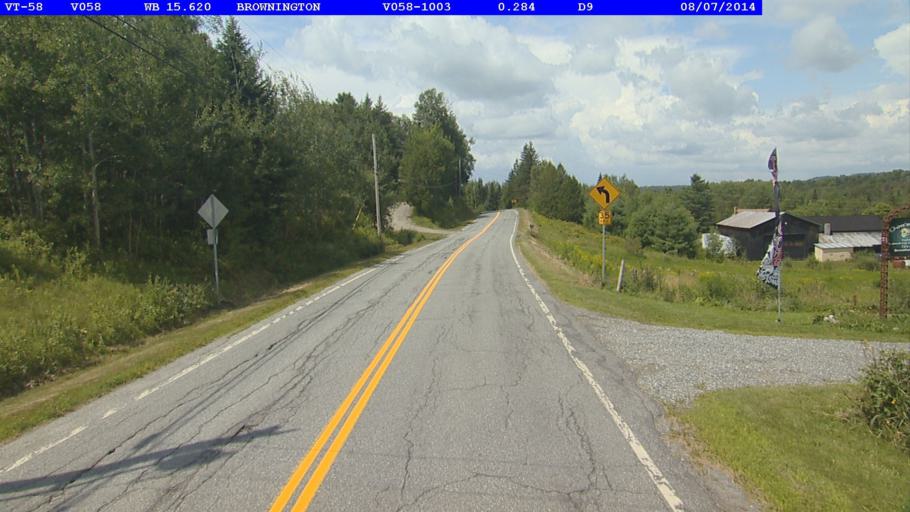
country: US
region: Vermont
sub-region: Orleans County
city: Newport
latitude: 44.8051
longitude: -72.1392
